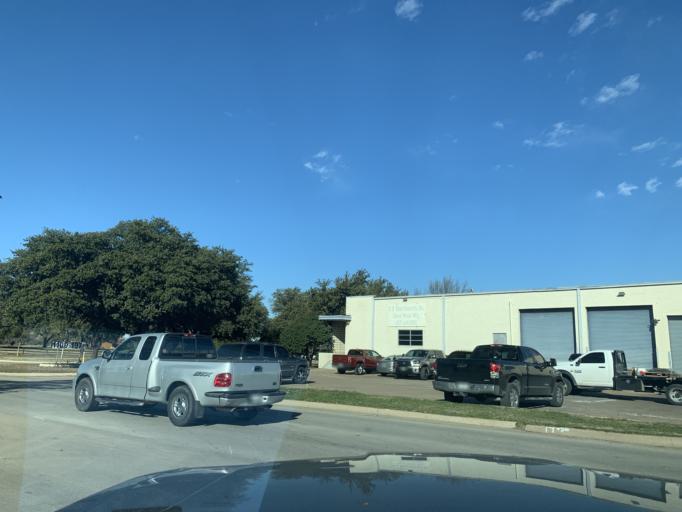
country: US
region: Texas
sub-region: Tarrant County
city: Arlington
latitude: 32.7617
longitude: -97.0573
